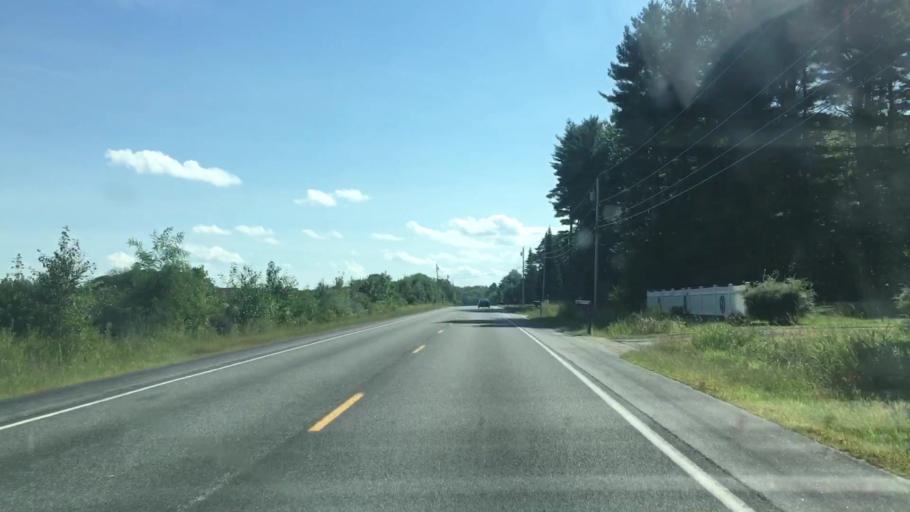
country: US
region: Maine
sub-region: Androscoggin County
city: Lisbon
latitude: 44.0631
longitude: -70.0850
